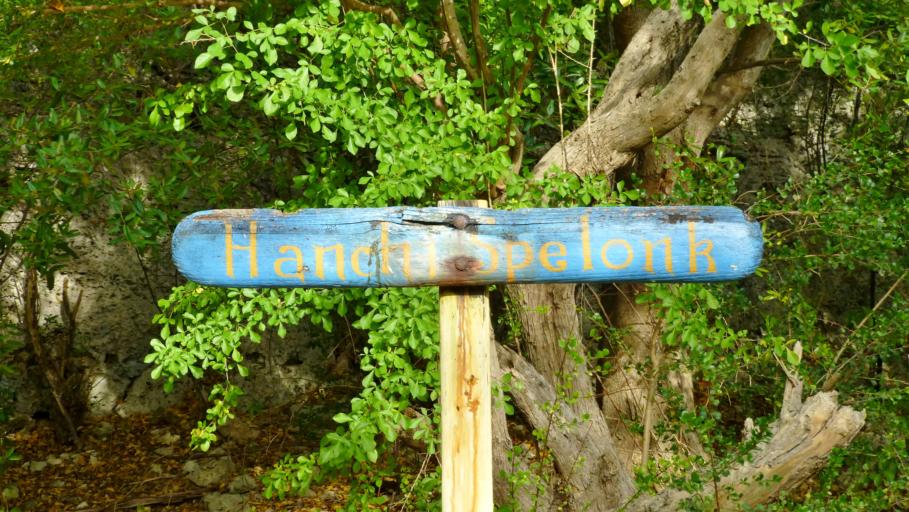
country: CW
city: Sint Michiel Liber
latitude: 12.1807
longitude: -68.9621
